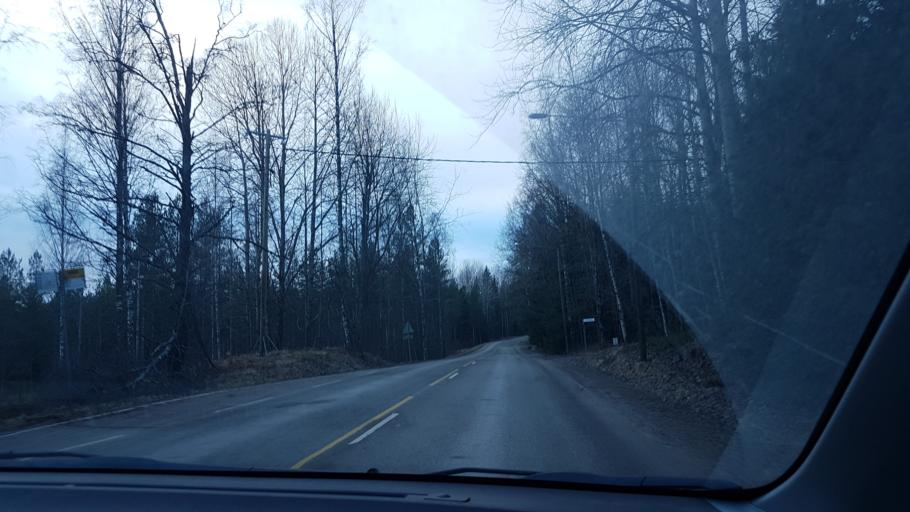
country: FI
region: Uusimaa
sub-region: Helsinki
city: Kauniainen
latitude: 60.3420
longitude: 24.7134
